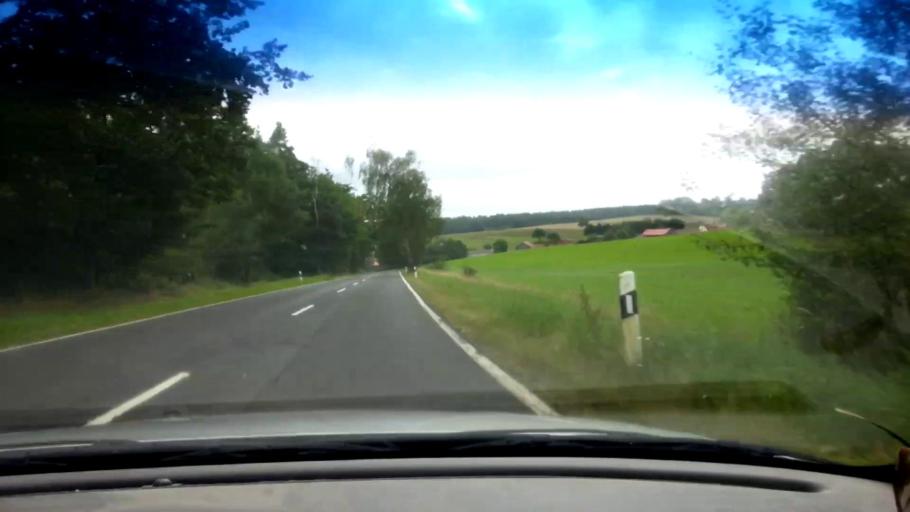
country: DE
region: Bavaria
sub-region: Upper Palatinate
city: Waldsassen
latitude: 50.0392
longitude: 12.2898
